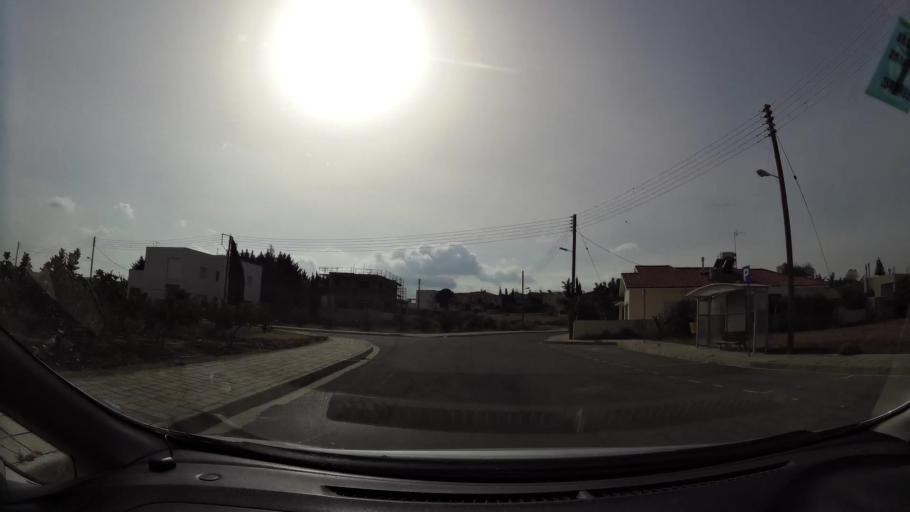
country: CY
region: Lefkosia
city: Geri
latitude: 35.0735
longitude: 33.3947
